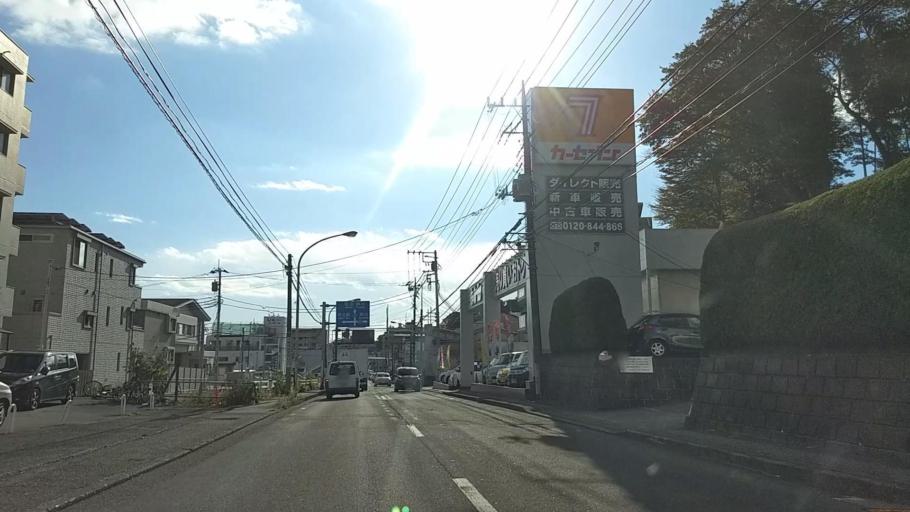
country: JP
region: Tokyo
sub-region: Machida-shi
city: Machida
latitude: 35.5923
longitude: 139.4976
